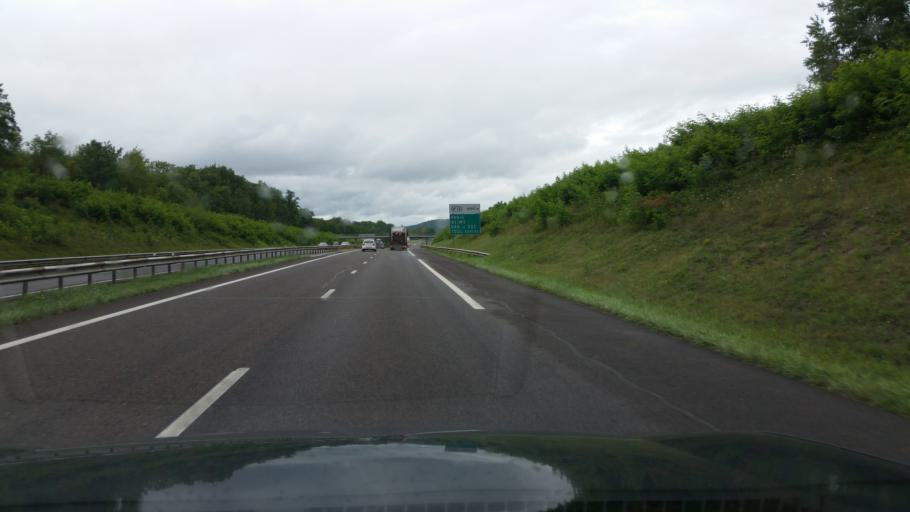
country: FR
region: Lorraine
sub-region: Departement de Meurthe-et-Moselle
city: Dommartin-les-Toul
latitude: 48.6391
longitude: 5.8807
